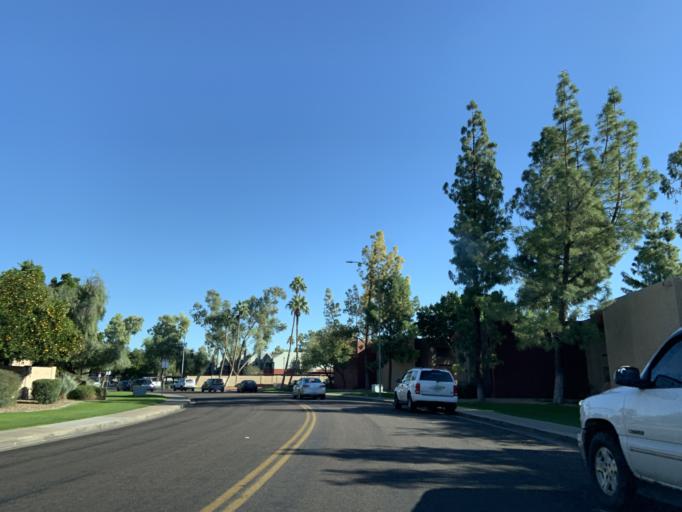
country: US
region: Arizona
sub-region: Maricopa County
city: Tempe
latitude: 33.3982
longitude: -111.8687
